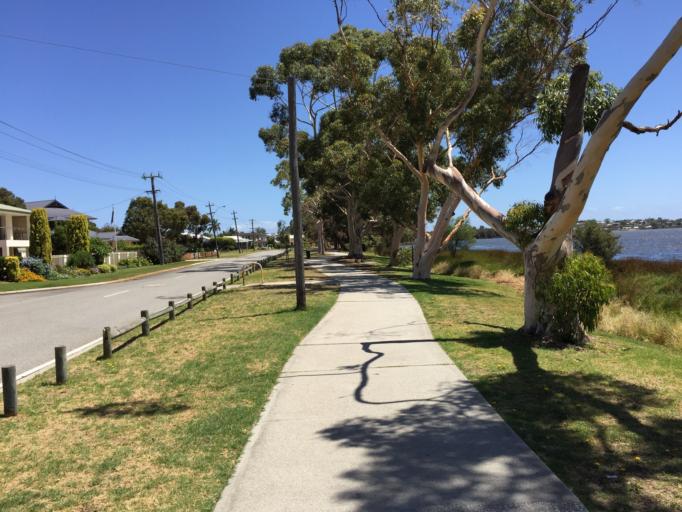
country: AU
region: Western Australia
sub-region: Canning
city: Wilson
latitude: -32.0234
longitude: 115.8911
